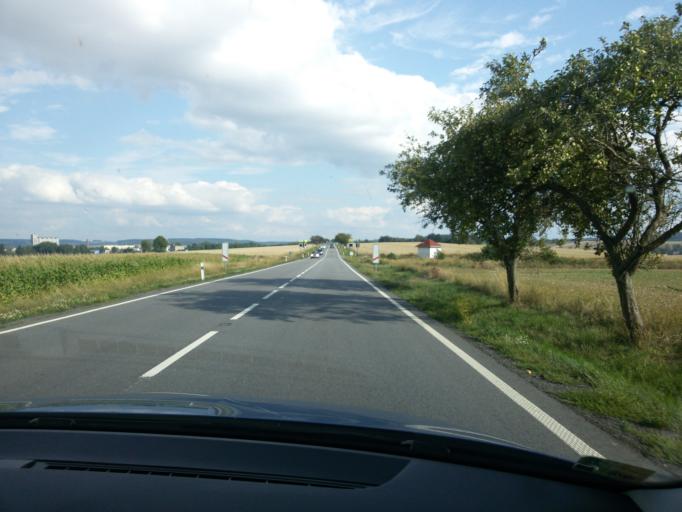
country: CZ
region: Pardubicky
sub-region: Okres Svitavy
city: Policka
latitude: 49.7227
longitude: 16.2353
